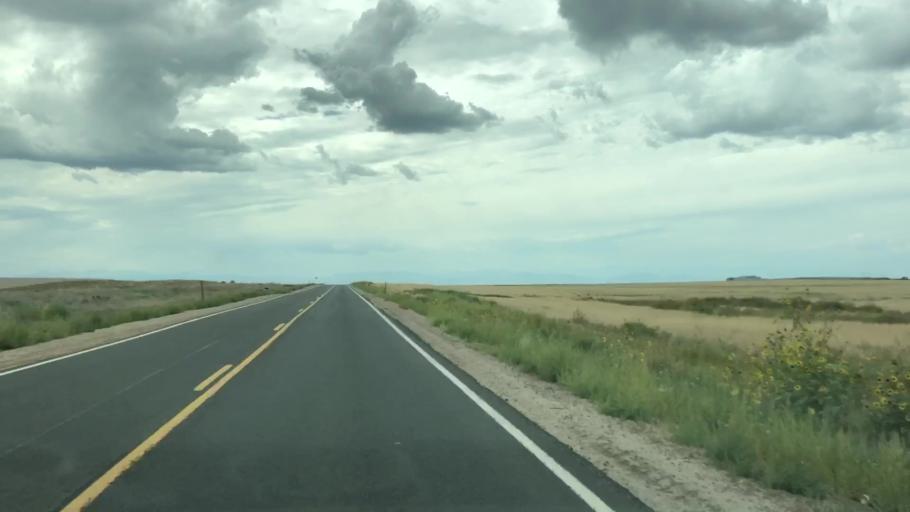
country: US
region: Colorado
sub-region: Adams County
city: Aurora
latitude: 39.7984
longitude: -104.7022
